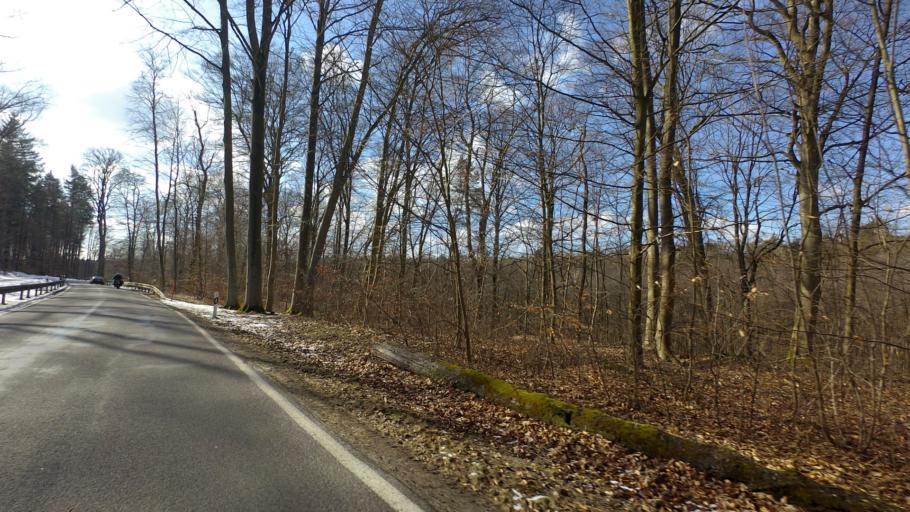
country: DE
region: Brandenburg
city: Wandlitz
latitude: 52.7588
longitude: 13.5413
